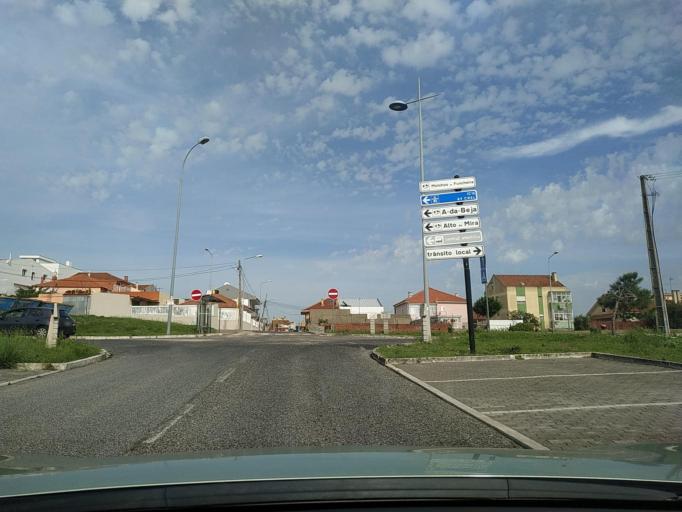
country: PT
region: Lisbon
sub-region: Amadora
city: Amadora
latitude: 38.7736
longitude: -9.2392
